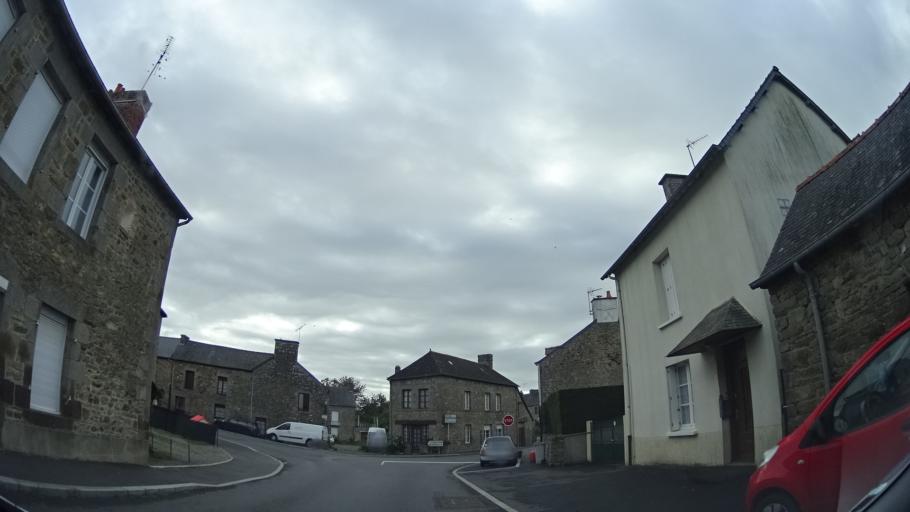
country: FR
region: Brittany
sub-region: Departement d'Ille-et-Vilaine
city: Dinge
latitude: 48.3579
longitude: -1.7129
